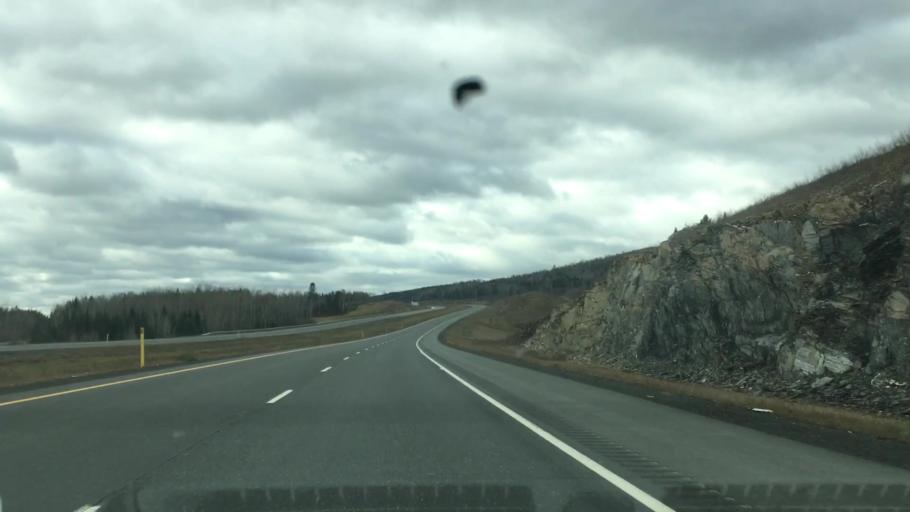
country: US
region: Maine
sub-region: Aroostook County
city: Fort Fairfield
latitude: 46.7344
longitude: -67.7203
